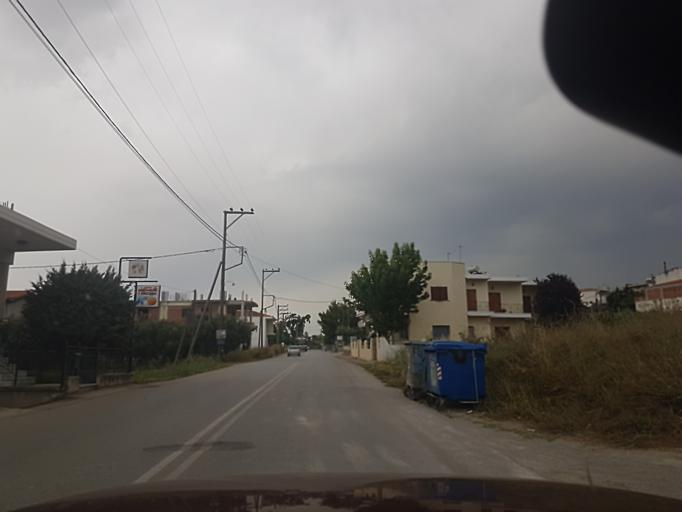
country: GR
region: Central Greece
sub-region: Nomos Evvoias
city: Mytikas
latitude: 38.4619
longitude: 23.6391
